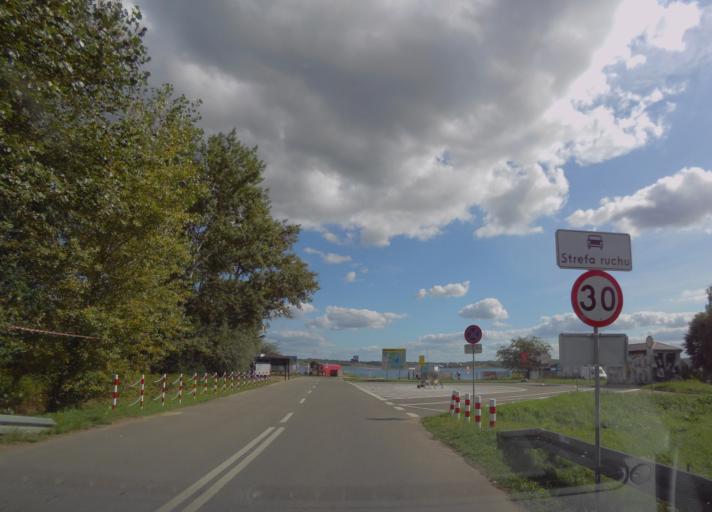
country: PL
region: Subcarpathian Voivodeship
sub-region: Tarnobrzeg
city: Tarnobrzeg
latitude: 50.5531
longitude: 21.6386
